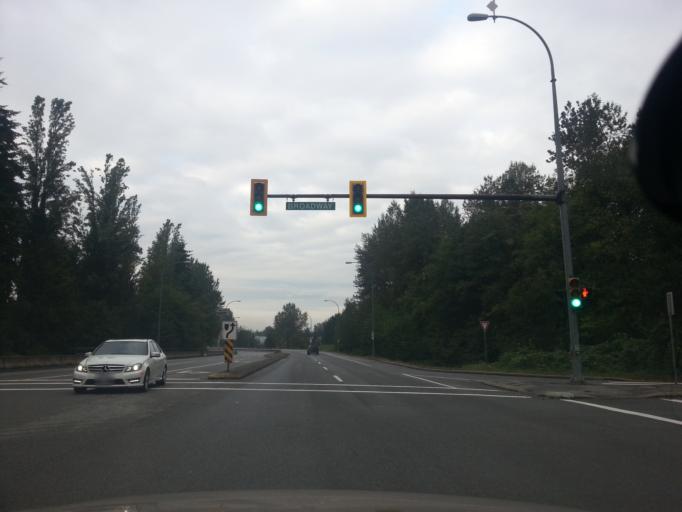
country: CA
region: British Columbia
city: Burnaby
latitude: 49.2601
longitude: -122.9088
